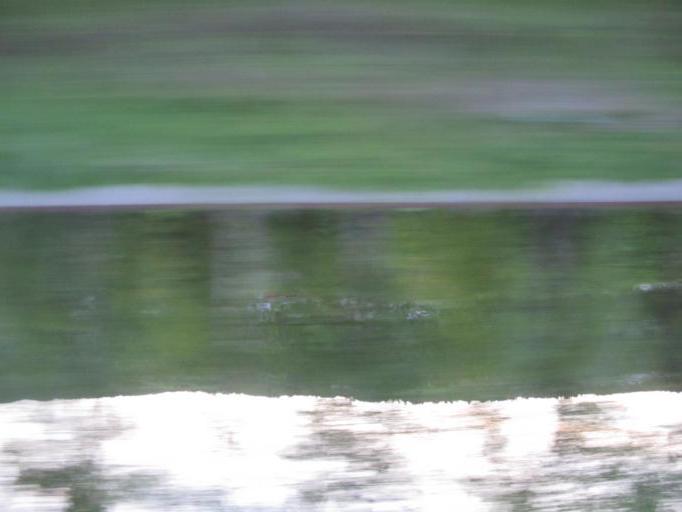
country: NO
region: Oppland
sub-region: Oyer
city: Tretten
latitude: 61.2640
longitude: 10.4065
